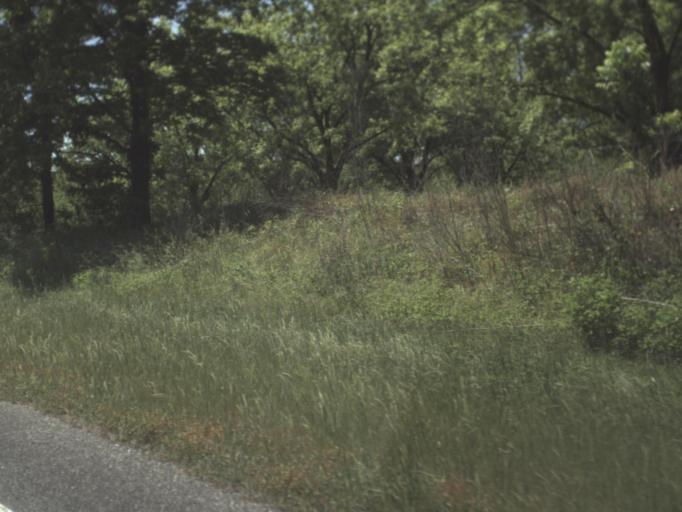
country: US
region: Florida
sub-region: Jefferson County
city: Monticello
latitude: 30.6376
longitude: -83.8738
